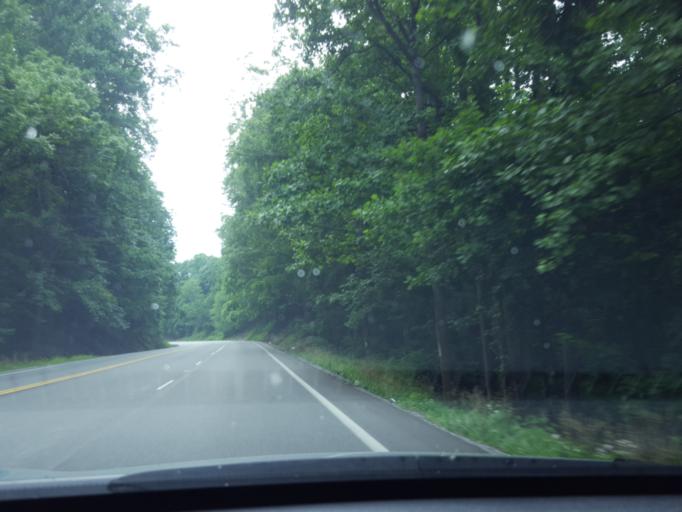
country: US
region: Virginia
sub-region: City of Waynesboro
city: Waynesboro
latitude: 38.0438
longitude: -78.8560
